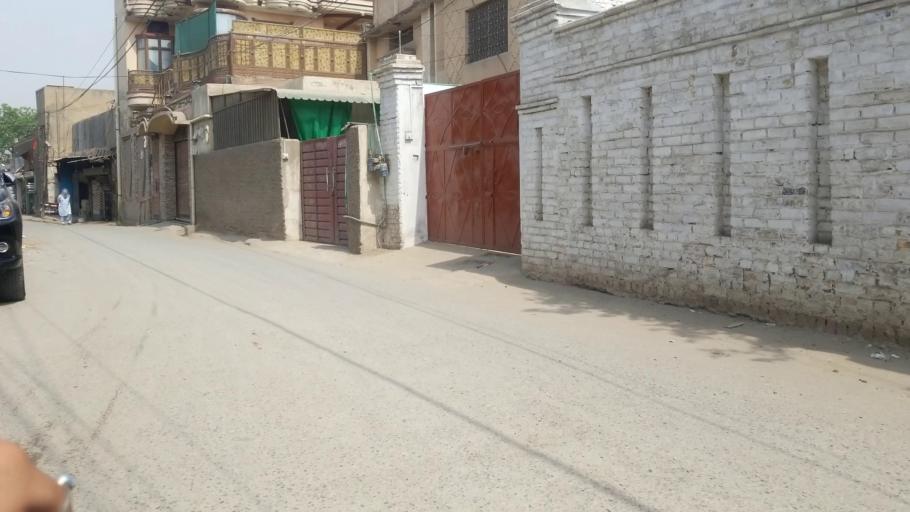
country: PK
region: Khyber Pakhtunkhwa
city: Peshawar
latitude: 33.9866
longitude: 71.5342
